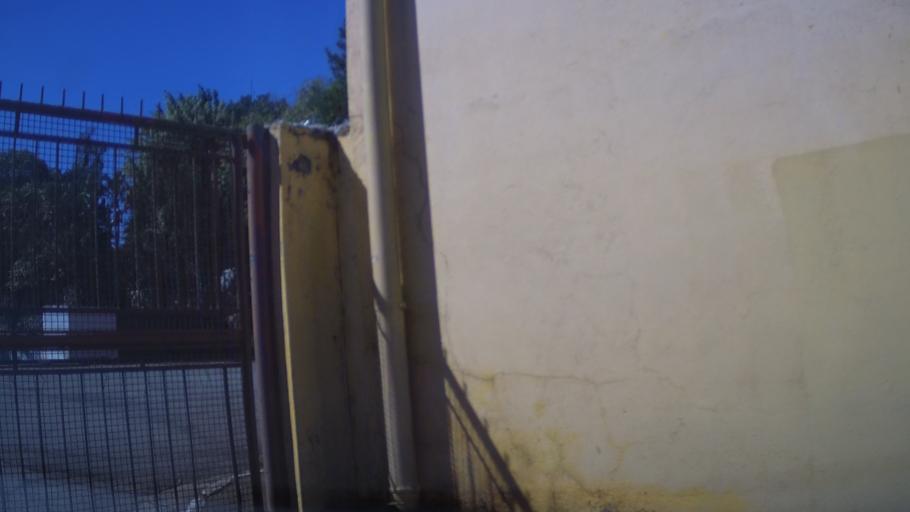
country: BR
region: Sao Paulo
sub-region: Sao Caetano Do Sul
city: Sao Caetano do Sul
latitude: -23.6444
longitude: -46.5704
